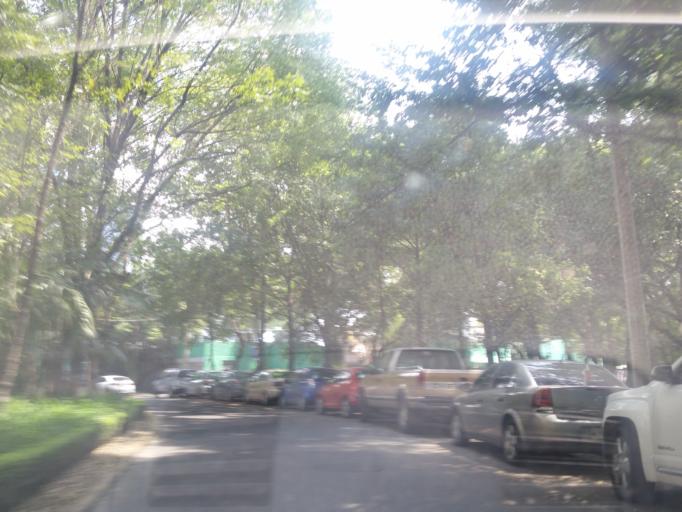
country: MX
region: Mexico City
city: Miguel Hidalgo
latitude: 19.4284
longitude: -99.1815
